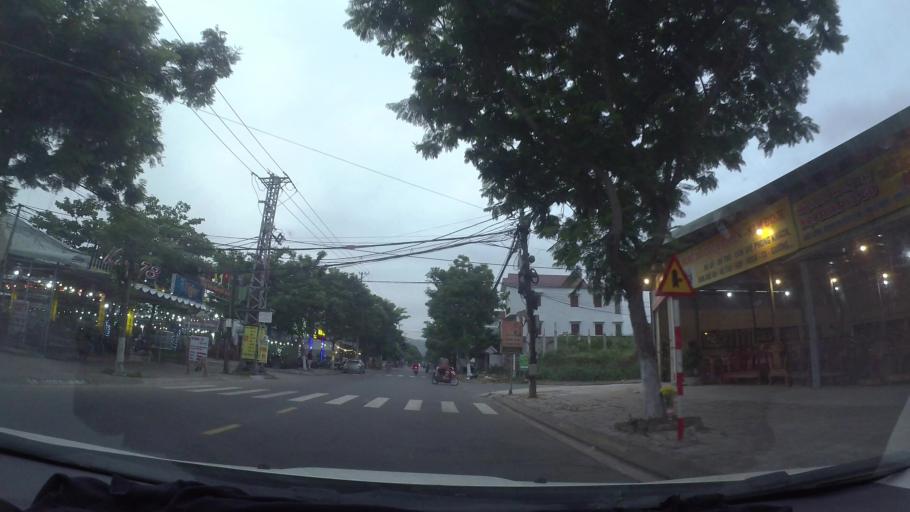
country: VN
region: Da Nang
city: Lien Chieu
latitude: 16.0871
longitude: 108.1533
